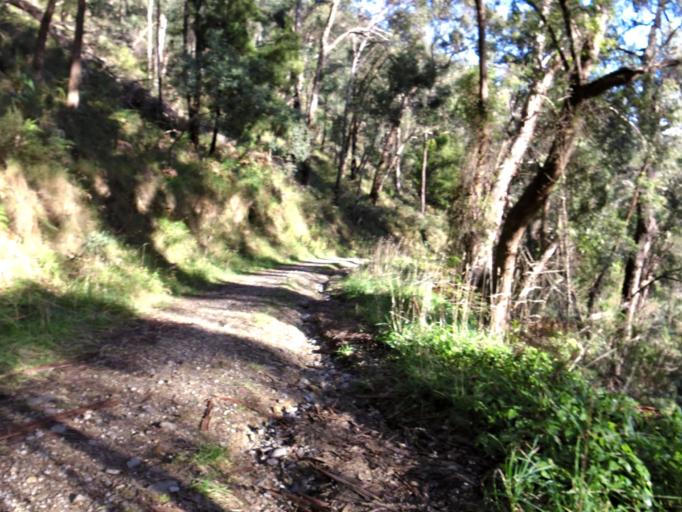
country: AU
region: Victoria
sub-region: Yarra Ranges
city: Kalorama
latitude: -37.8180
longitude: 145.3624
